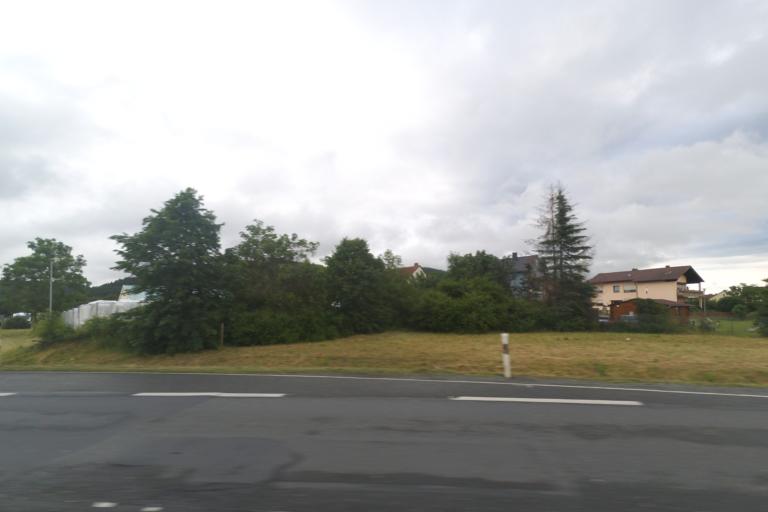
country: DE
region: Bavaria
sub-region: Upper Franconia
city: Marktrodach
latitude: 50.2552
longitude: 11.3949
